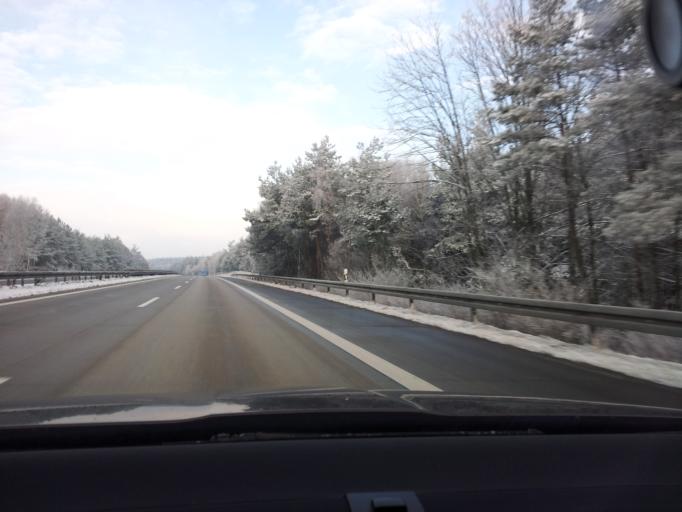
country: DE
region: Brandenburg
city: Heiligengrabe
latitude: 53.1539
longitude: 12.4000
